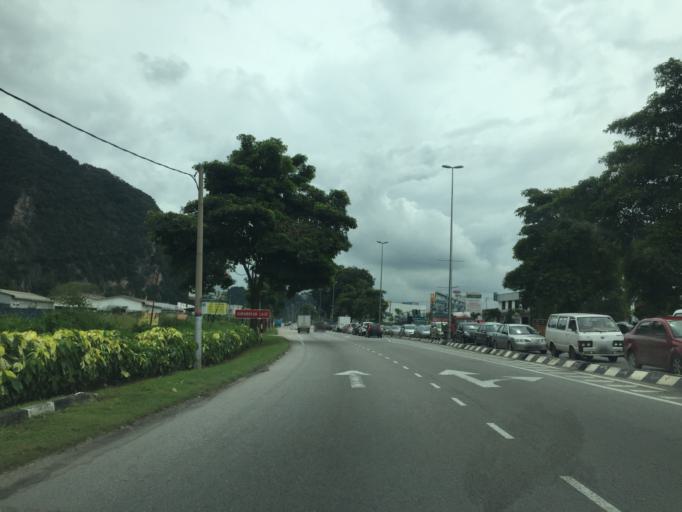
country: MY
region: Perak
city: Ipoh
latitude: 4.5586
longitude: 101.1125
